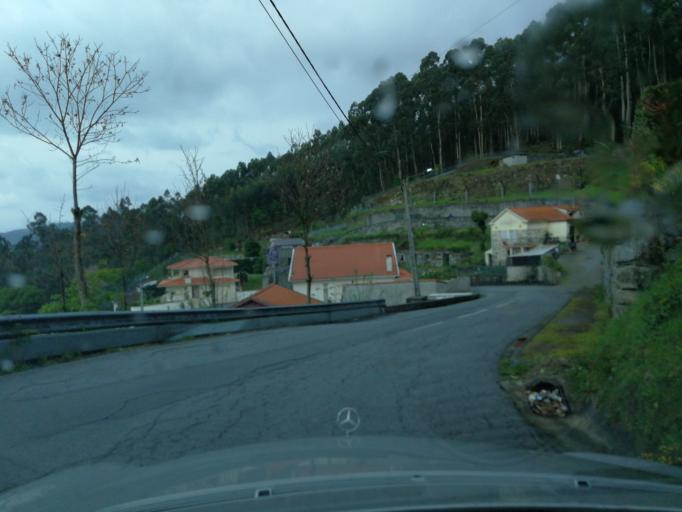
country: PT
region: Braga
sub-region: Vila Nova de Famalicao
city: Joane
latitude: 41.4774
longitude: -8.4246
